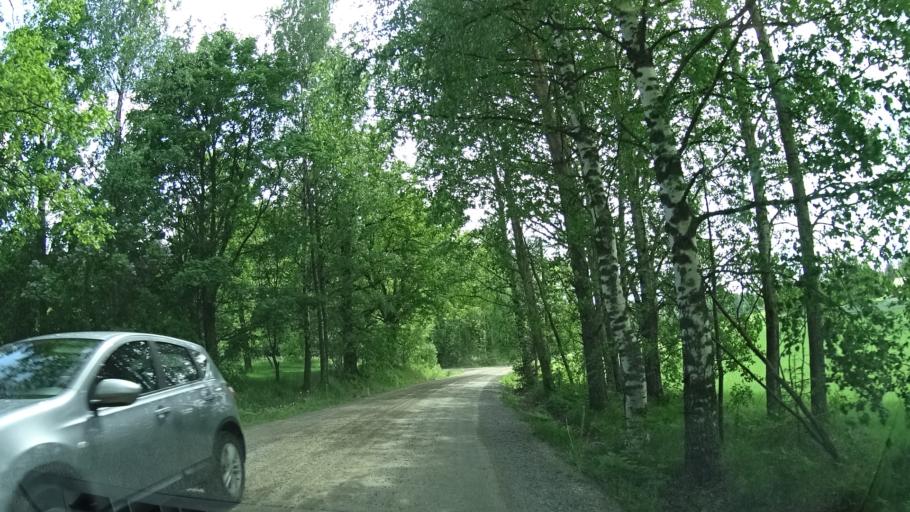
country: FI
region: Uusimaa
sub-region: Helsinki
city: Siuntio
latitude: 60.2202
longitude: 24.3027
